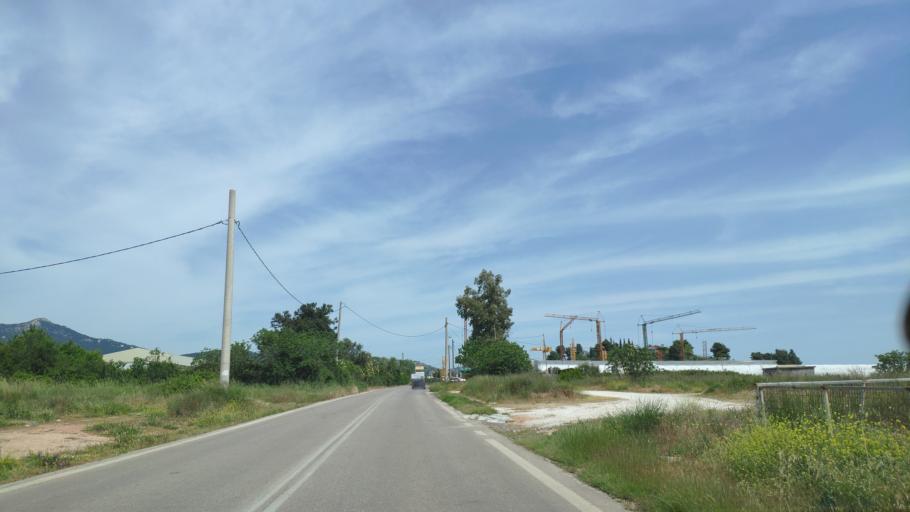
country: GR
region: Attica
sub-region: Nomarchia Anatolikis Attikis
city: Afidnes
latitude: 38.1809
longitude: 23.8568
